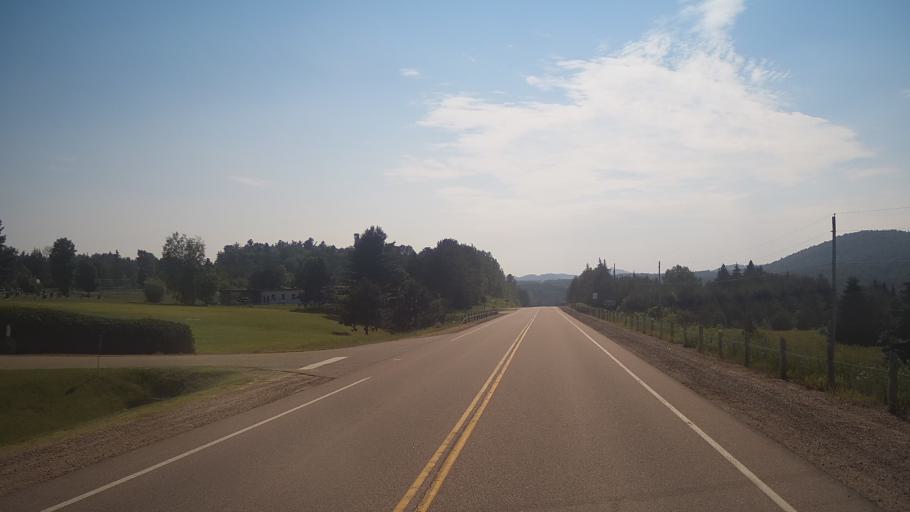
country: CA
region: Ontario
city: Petawawa
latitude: 45.5157
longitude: -77.5482
